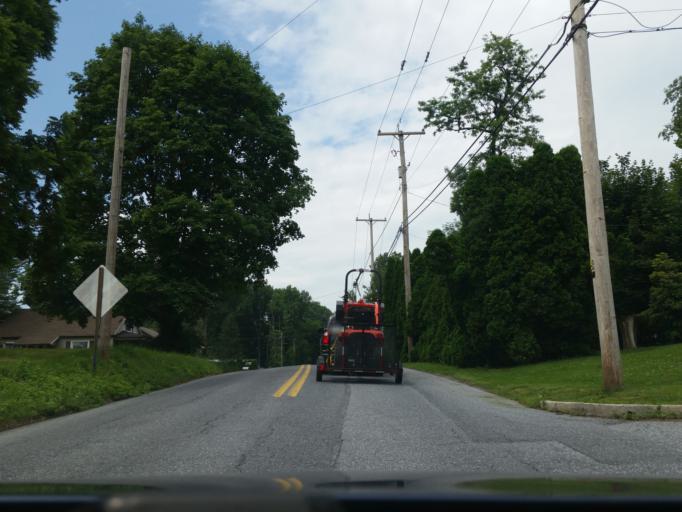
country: US
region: Pennsylvania
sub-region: Lebanon County
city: Sand Hill
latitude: 40.3796
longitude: -76.4433
